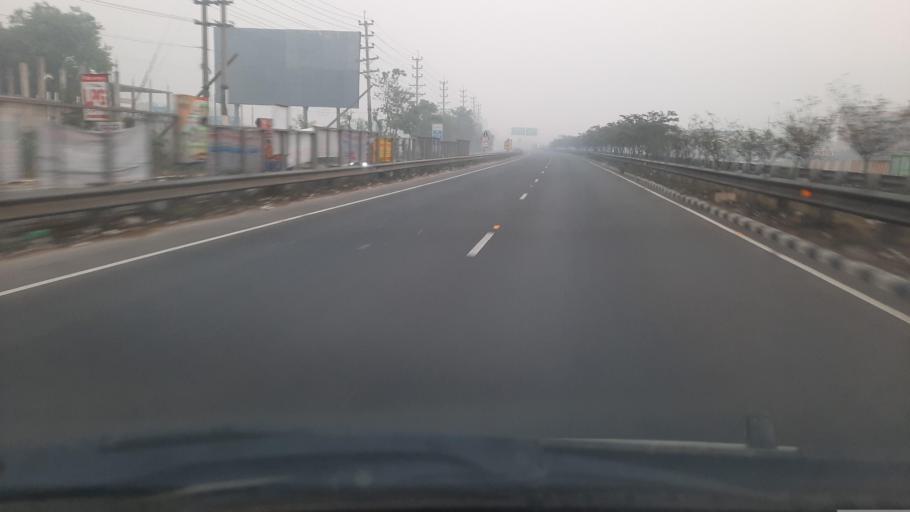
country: BD
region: Dhaka
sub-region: Dhaka
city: Dhaka
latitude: 23.6519
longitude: 90.3508
